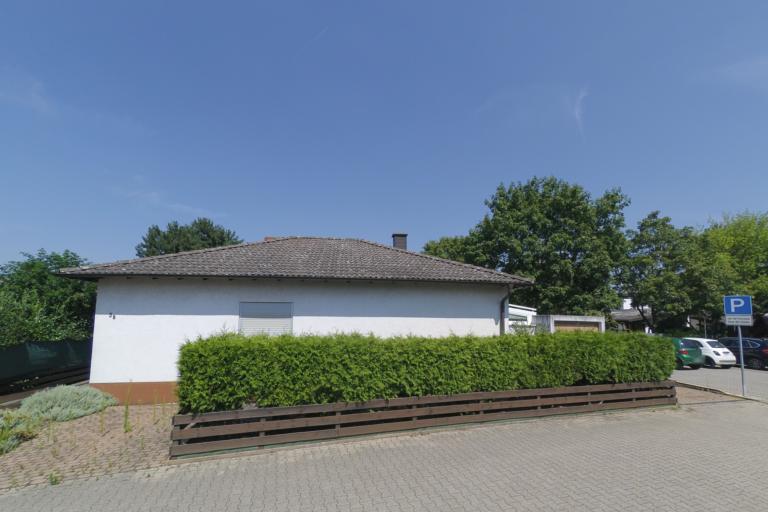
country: DE
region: Rheinland-Pfalz
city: Mutterstadt
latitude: 49.4393
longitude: 8.3659
